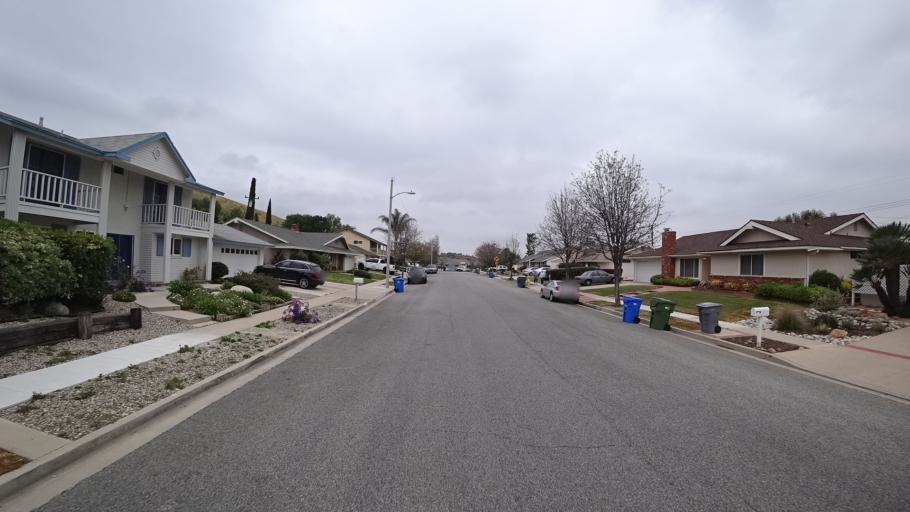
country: US
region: California
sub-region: Ventura County
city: Thousand Oaks
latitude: 34.2036
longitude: -118.8721
